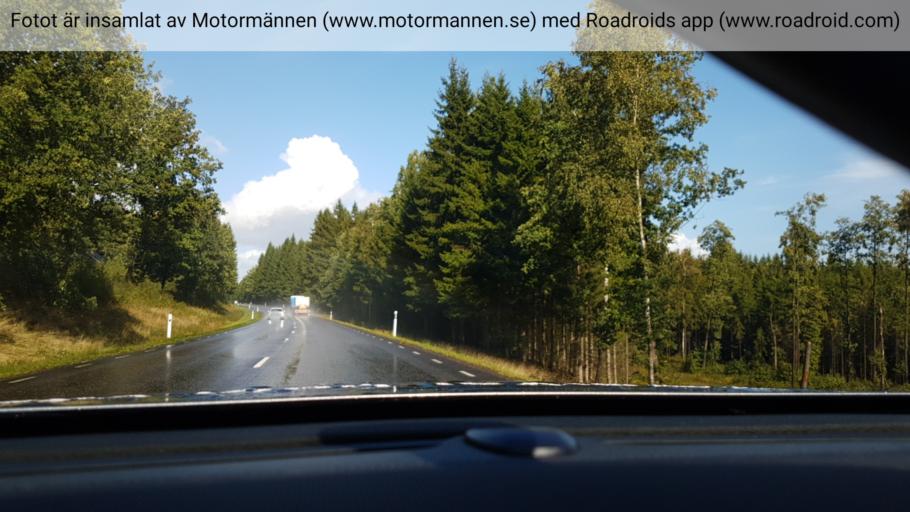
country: SE
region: Vaestra Goetaland
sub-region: Alingsas Kommun
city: Sollebrunn
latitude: 58.0237
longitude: 12.4590
